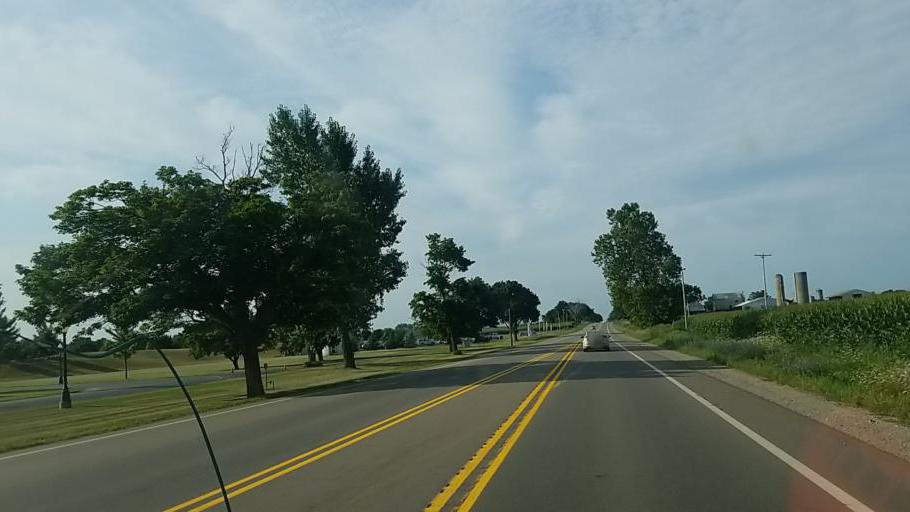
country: US
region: Michigan
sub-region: Ionia County
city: Ionia
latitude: 42.9143
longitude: -85.0748
